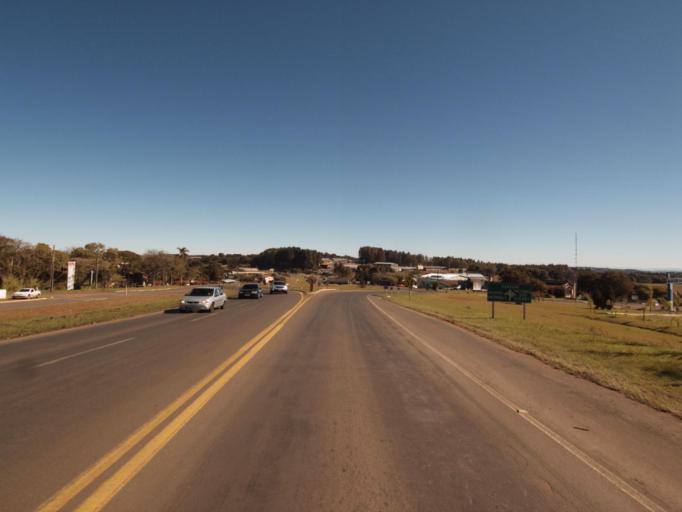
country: BR
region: Santa Catarina
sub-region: Xanxere
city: Xanxere
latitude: -26.8569
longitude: -52.2610
